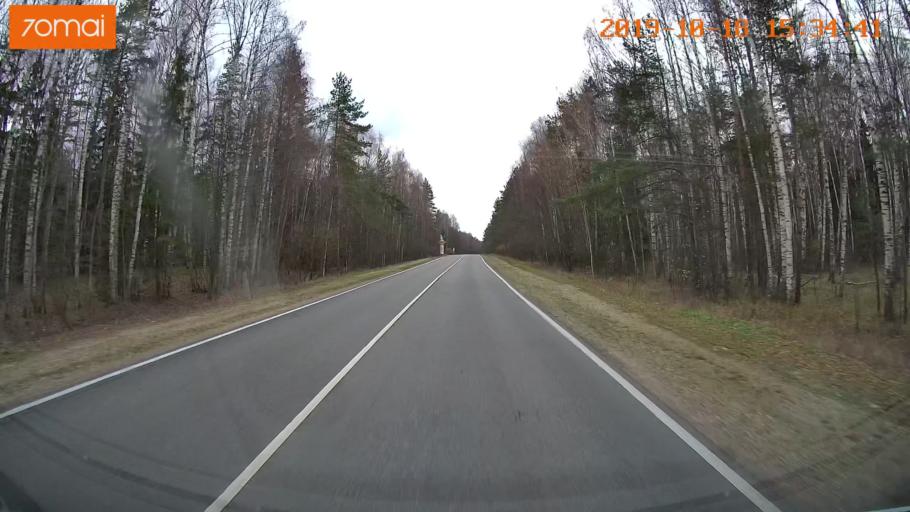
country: RU
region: Vladimir
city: Anopino
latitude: 55.8572
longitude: 40.6390
